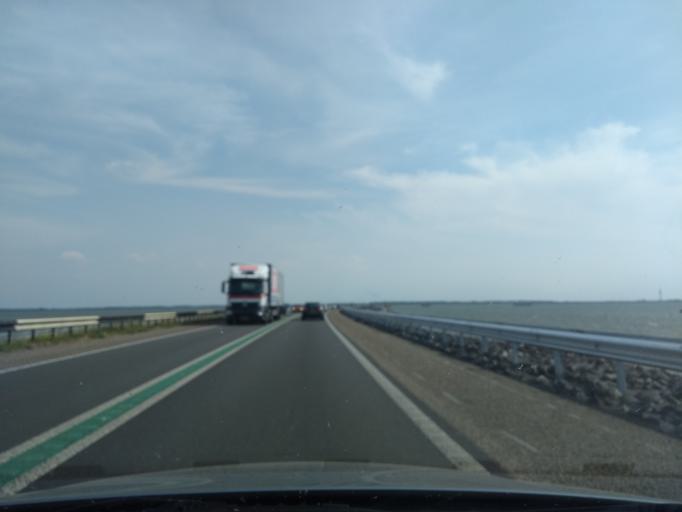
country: NL
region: Flevoland
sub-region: Gemeente Lelystad
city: Lelystad
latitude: 52.5922
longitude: 5.4570
